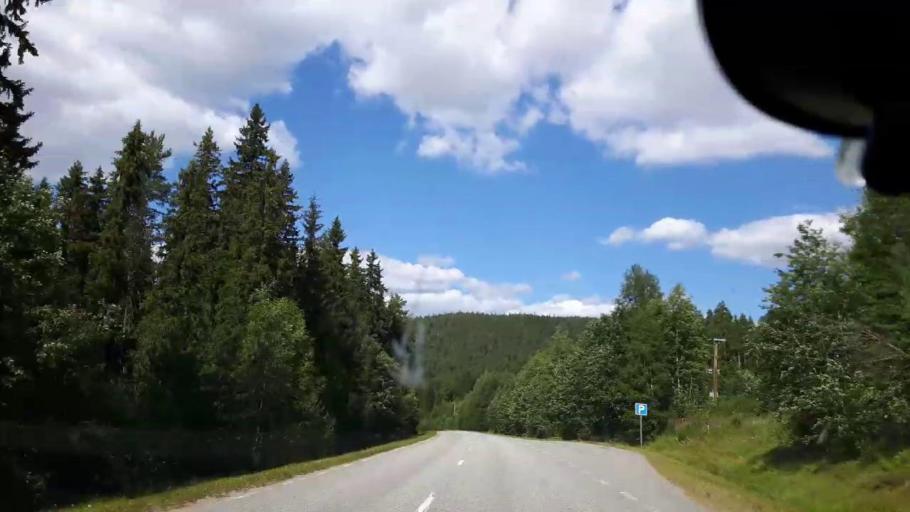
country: SE
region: Vaesternorrland
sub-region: Ange Kommun
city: Fransta
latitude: 62.7355
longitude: 16.3309
